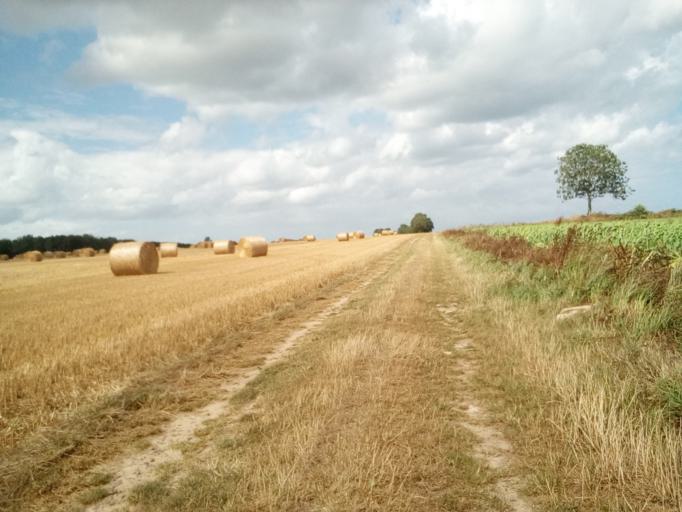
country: FR
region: Lower Normandy
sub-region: Departement du Calvados
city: Creully
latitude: 49.2961
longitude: -0.5697
